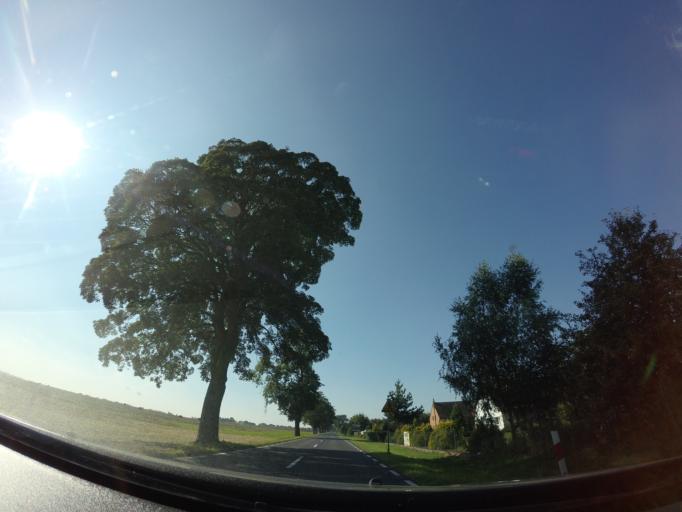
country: PL
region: West Pomeranian Voivodeship
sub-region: Powiat stargardzki
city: Stargard Szczecinski
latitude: 53.3733
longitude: 15.0768
